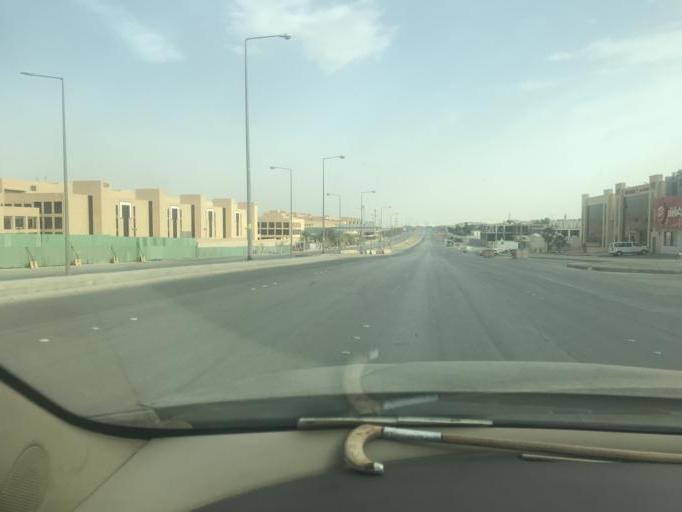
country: SA
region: Ar Riyad
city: Riyadh
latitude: 24.8157
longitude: 46.6887
